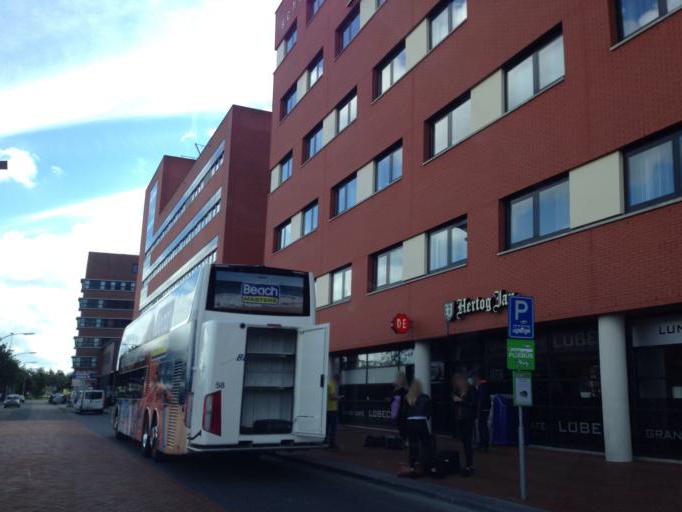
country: NL
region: Overijssel
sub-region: Gemeente Zwolle
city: Zwolle
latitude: 52.5038
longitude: 6.0901
